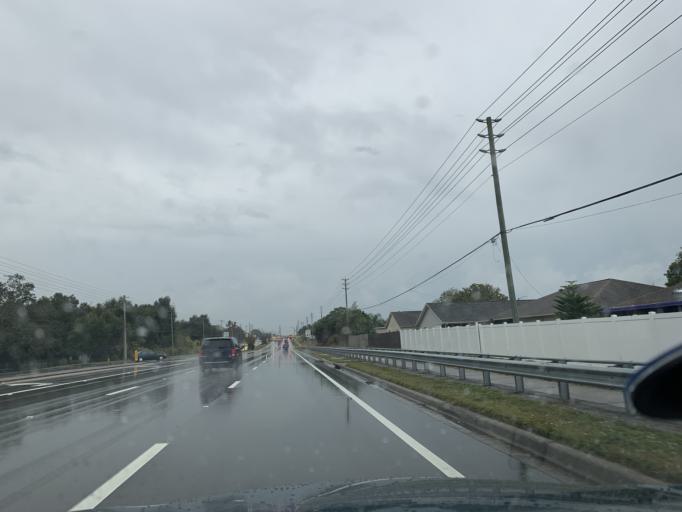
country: US
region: Florida
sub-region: Pasco County
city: Bayonet Point
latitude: 28.3236
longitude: -82.6662
